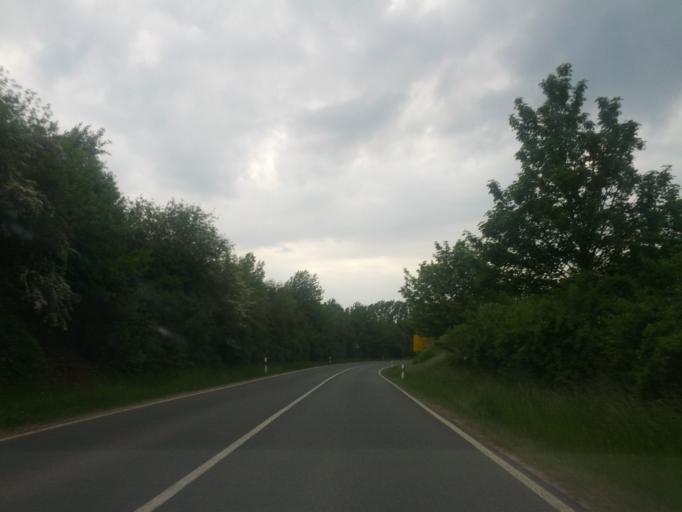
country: DE
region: Thuringia
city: Ernstroda
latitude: 50.8882
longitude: 10.6524
